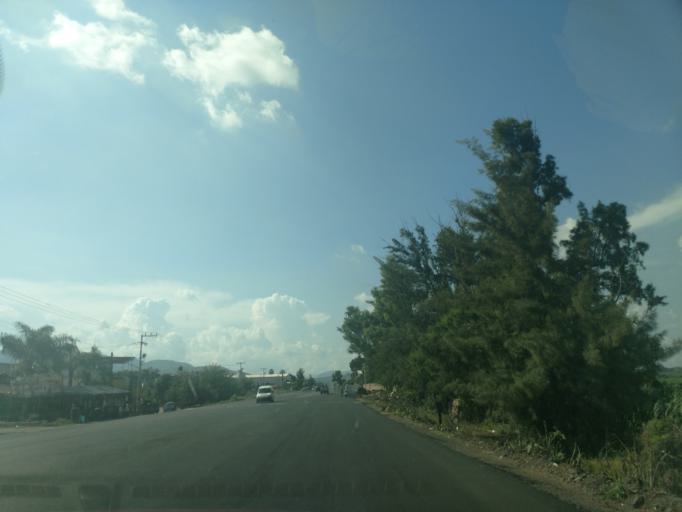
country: MX
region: Jalisco
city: Ahualulco de Mercado
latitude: 20.7012
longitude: -103.9668
